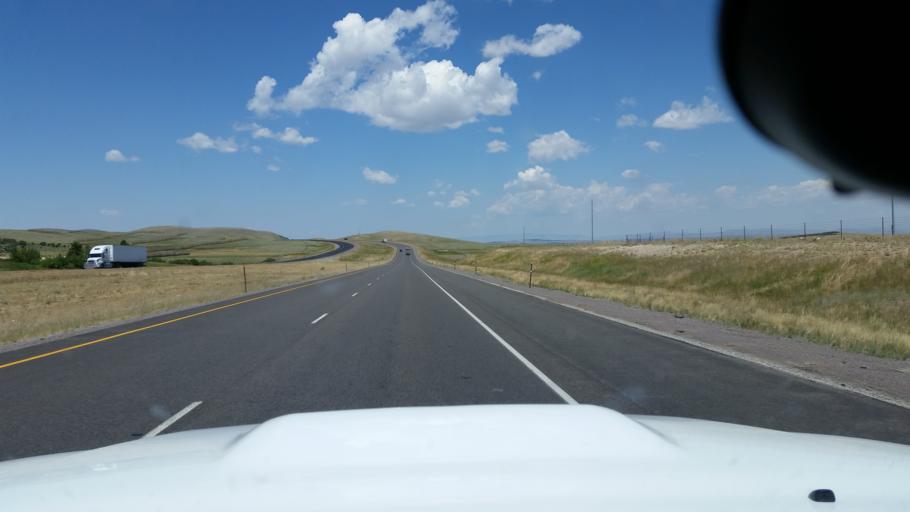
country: US
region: Wyoming
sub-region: Carbon County
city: Saratoga
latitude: 41.6128
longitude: -106.2330
